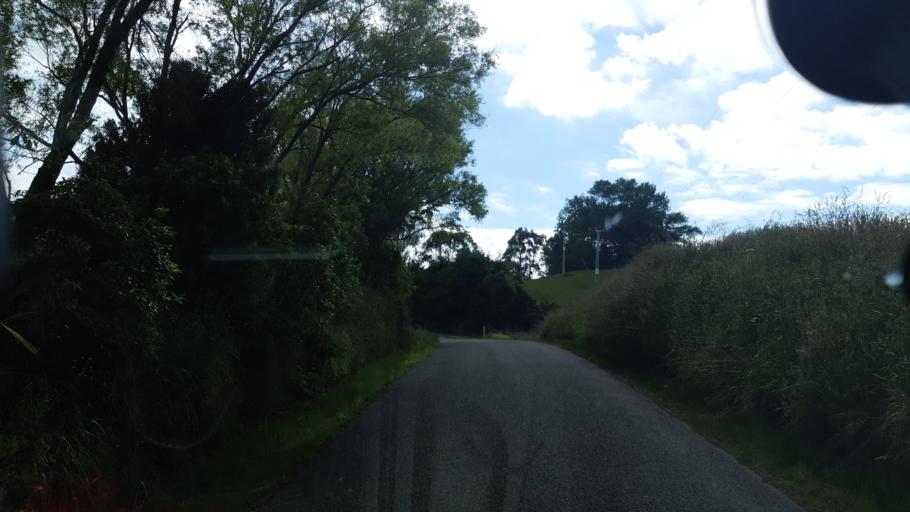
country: NZ
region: Manawatu-Wanganui
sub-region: Rangitikei District
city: Bulls
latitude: -39.9647
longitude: 175.4636
